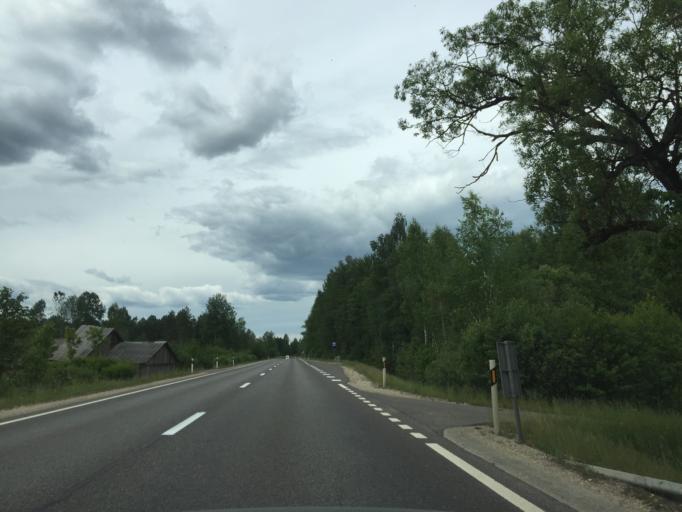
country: LV
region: Livani
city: Livani
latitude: 56.5425
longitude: 26.1244
